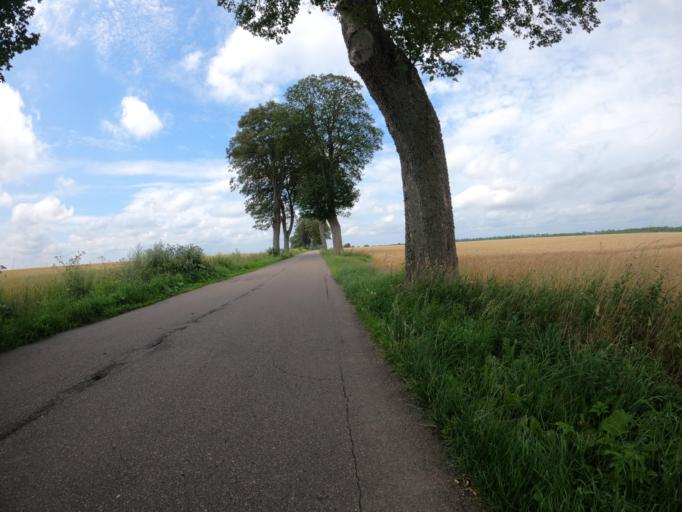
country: PL
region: West Pomeranian Voivodeship
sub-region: Powiat szczecinecki
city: Grzmiaca
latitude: 53.7898
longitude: 16.4824
